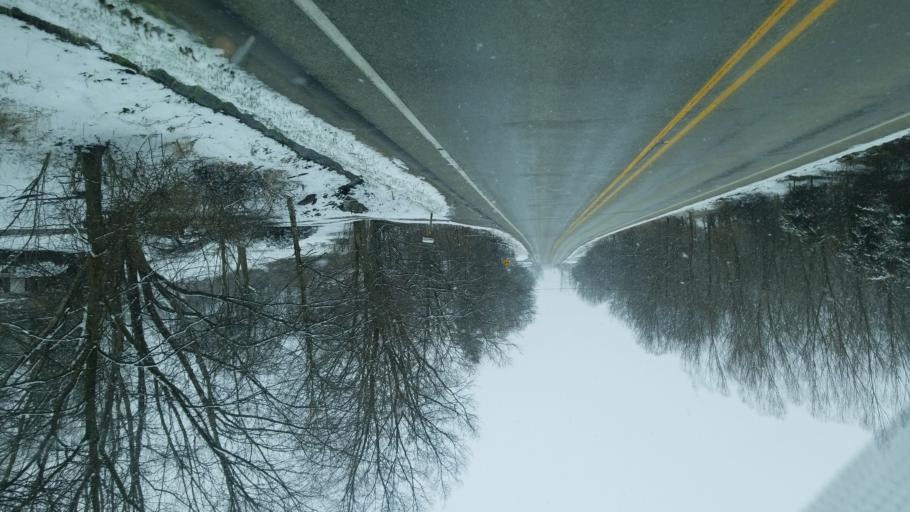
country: US
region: Indiana
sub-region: Wayne County
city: Centerville
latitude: 39.9196
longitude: -84.9546
